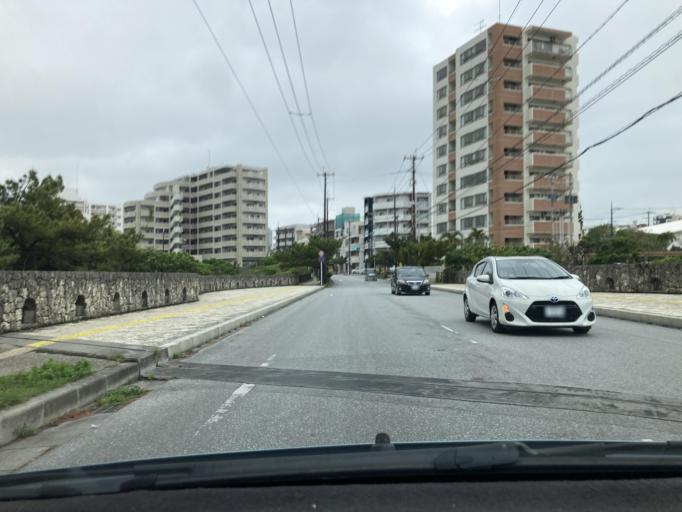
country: JP
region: Okinawa
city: Naha-shi
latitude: 26.2357
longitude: 127.6962
